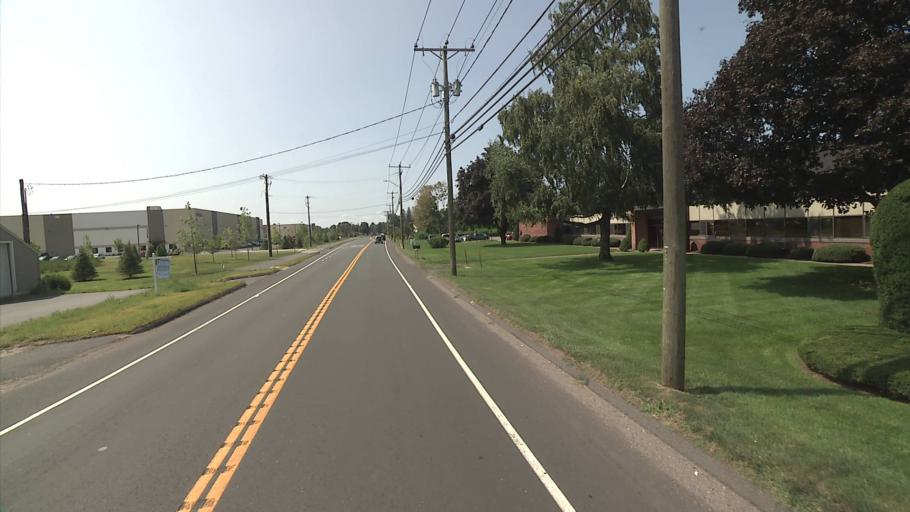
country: US
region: Connecticut
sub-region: Hartford County
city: South Windsor
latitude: 41.8554
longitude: -72.5937
